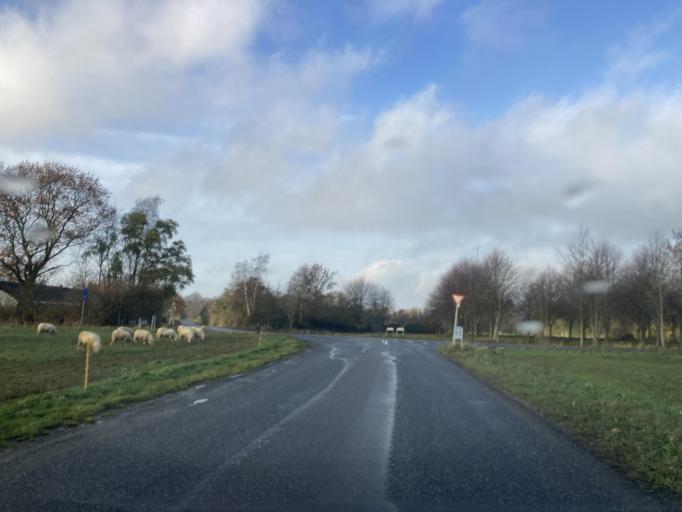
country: DK
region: Zealand
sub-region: Lolland Kommune
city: Rodby
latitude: 54.6885
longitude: 11.3929
